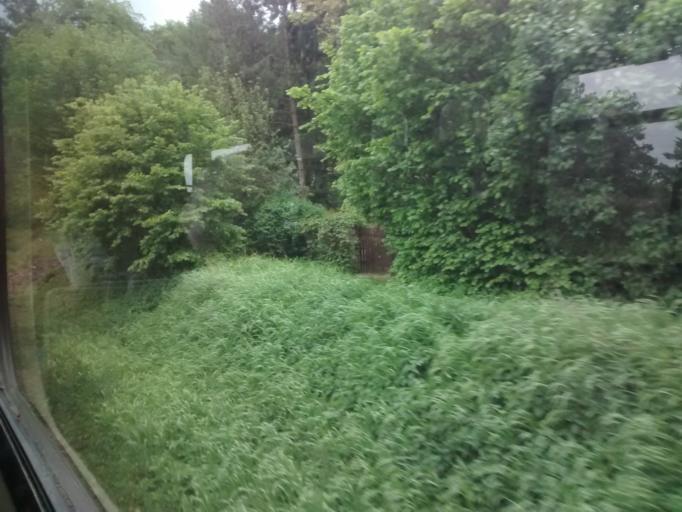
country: DE
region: Brandenburg
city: Glienicke
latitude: 52.6691
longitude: 13.3234
